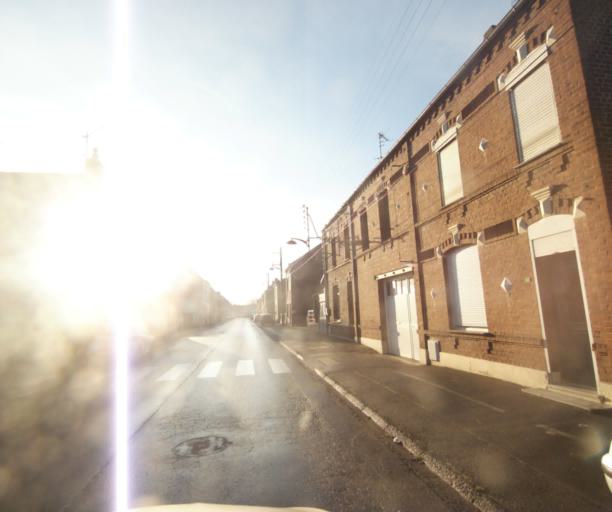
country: FR
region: Nord-Pas-de-Calais
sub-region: Departement du Nord
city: Onnaing
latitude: 50.3892
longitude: 3.5953
